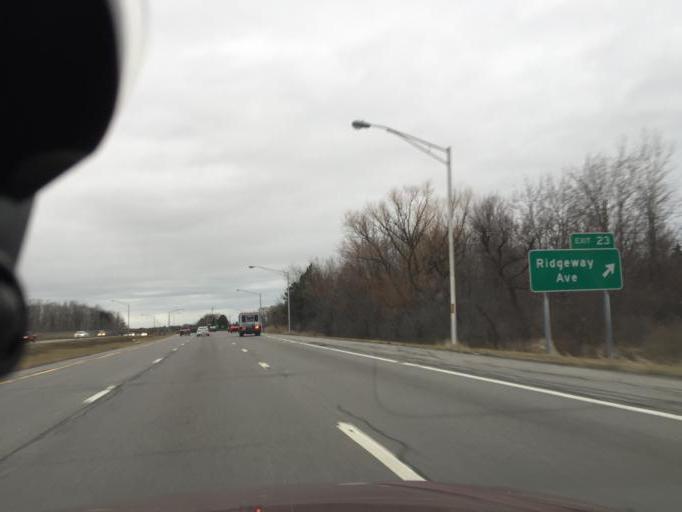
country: US
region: New York
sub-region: Monroe County
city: North Gates
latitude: 43.1873
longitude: -77.6831
